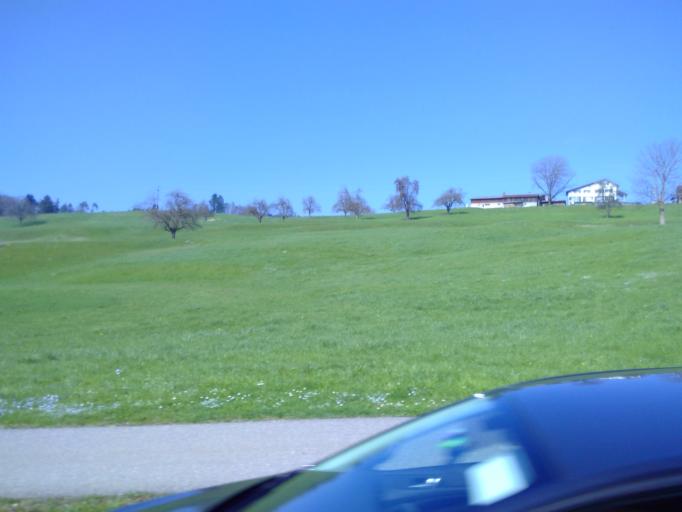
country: CH
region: Saint Gallen
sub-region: Wahlkreis See-Gaster
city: Eschenbach
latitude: 47.2339
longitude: 8.9091
